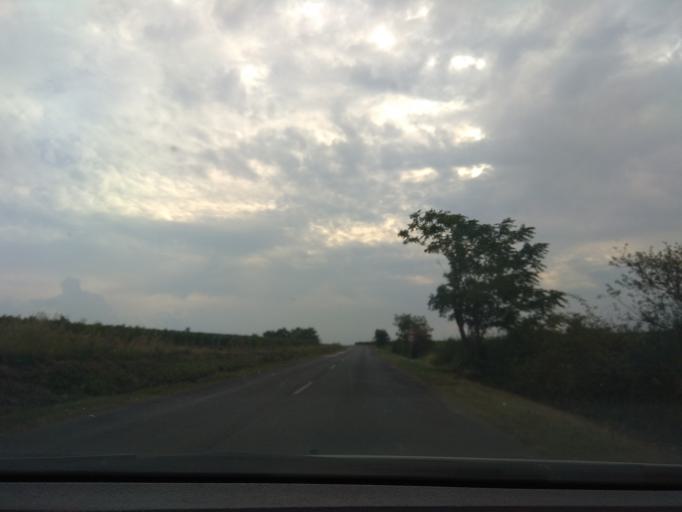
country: HU
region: Heves
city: Egerszalok
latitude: 47.8833
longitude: 20.3423
